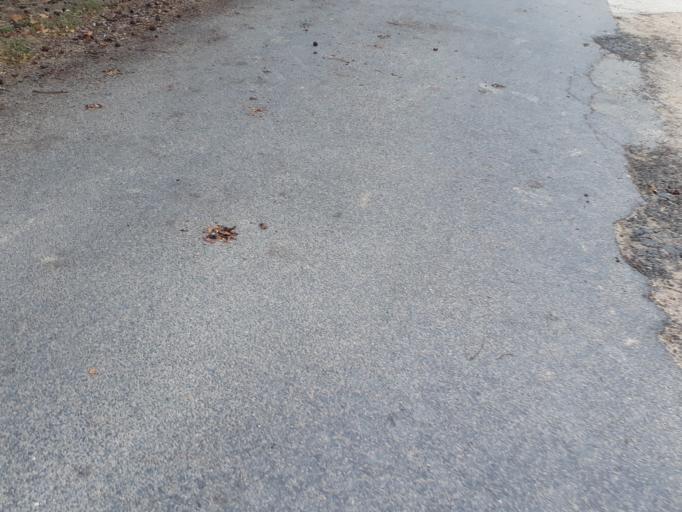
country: FR
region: Centre
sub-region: Departement du Loiret
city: Saint-Benoit-sur-Loire
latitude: 47.7914
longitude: 2.3090
